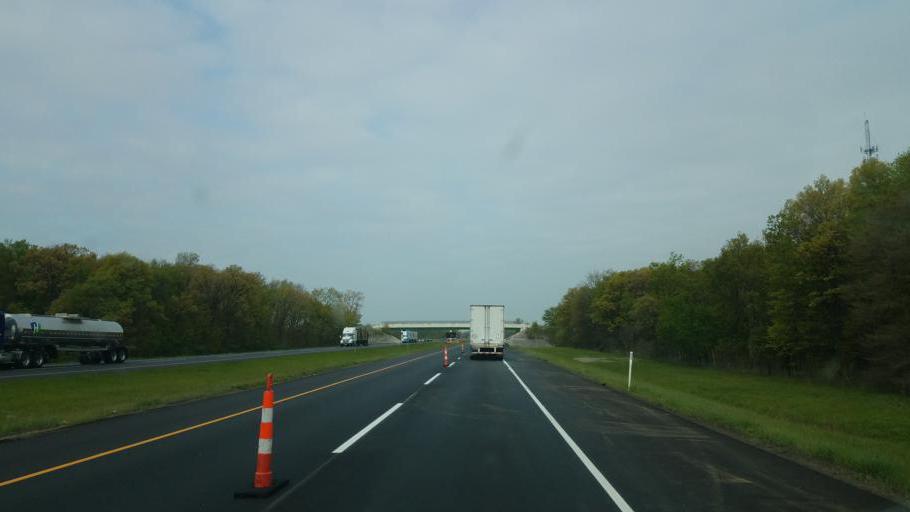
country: US
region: Indiana
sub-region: Saint Joseph County
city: Granger
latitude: 41.7314
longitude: -86.0775
